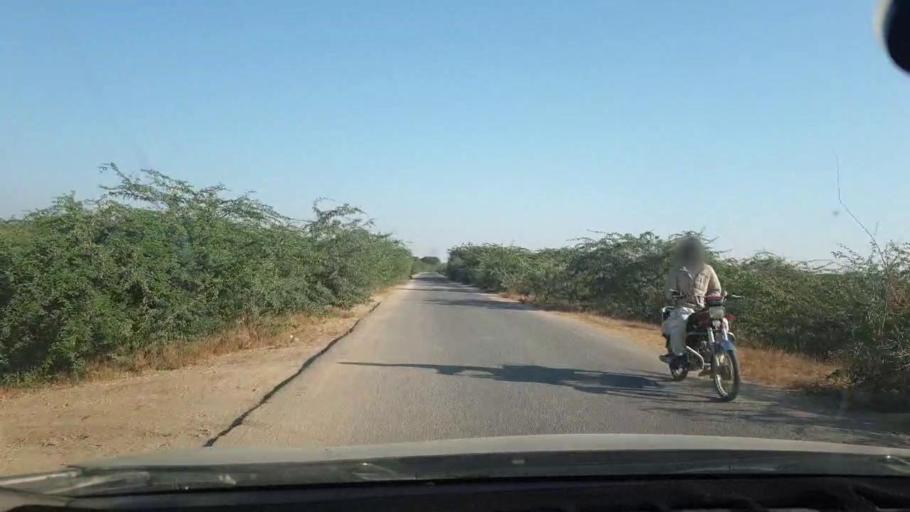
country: PK
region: Sindh
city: Malir Cantonment
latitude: 25.1461
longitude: 67.1873
